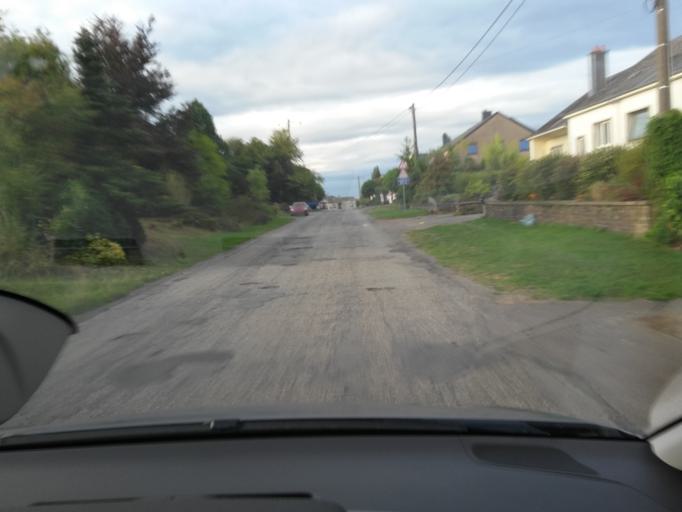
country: BE
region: Wallonia
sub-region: Province du Luxembourg
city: Arlon
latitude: 49.7089
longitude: 5.8157
